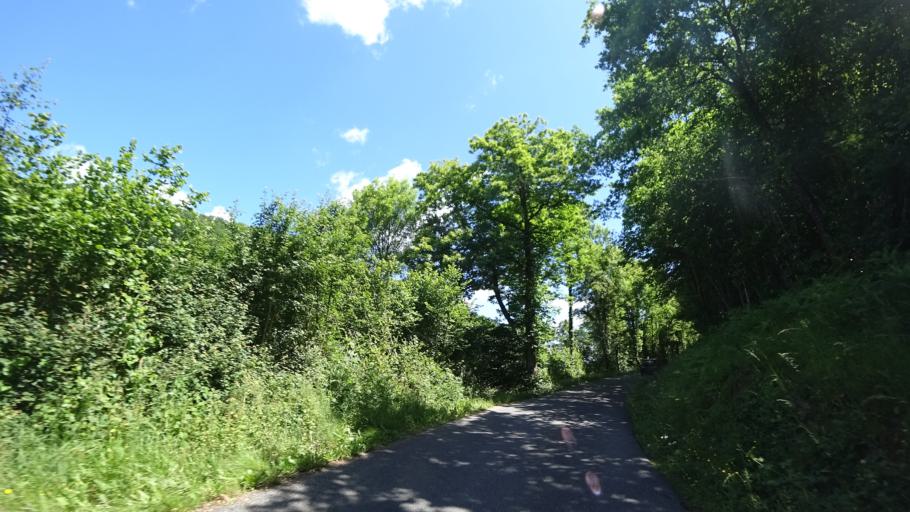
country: FR
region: Midi-Pyrenees
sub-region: Departement de l'Aveyron
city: Colombies
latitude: 44.3759
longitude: 2.3117
